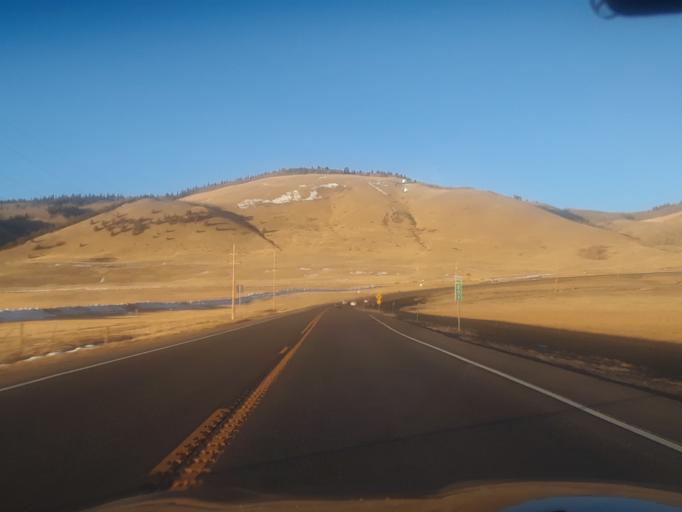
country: US
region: Colorado
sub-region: Summit County
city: Breckenridge
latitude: 39.3994
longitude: -105.7822
